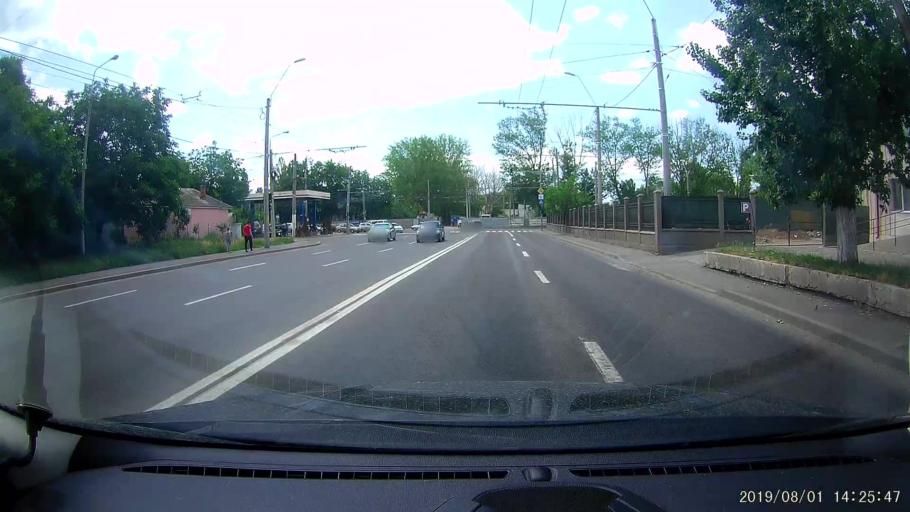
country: RO
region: Galati
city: Galati
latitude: 45.4652
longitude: 28.0345
